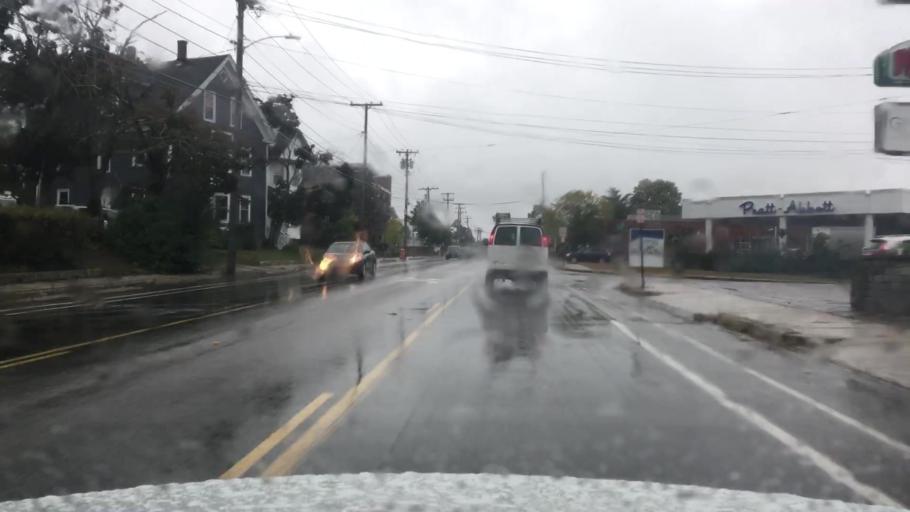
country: US
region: Maine
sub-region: Cumberland County
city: Portland
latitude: 43.6832
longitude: -70.2908
